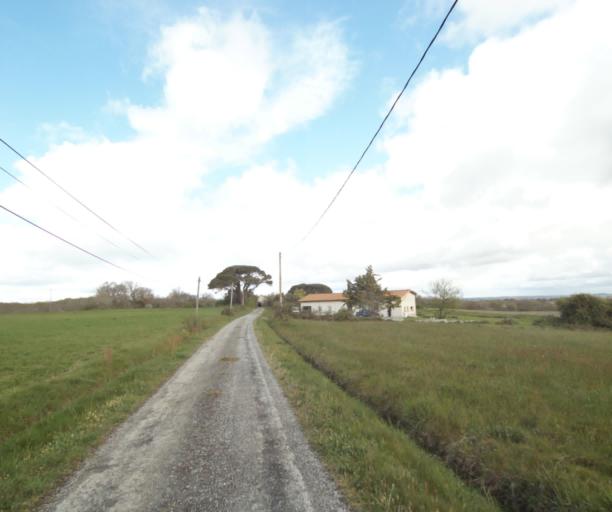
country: FR
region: Midi-Pyrenees
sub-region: Departement de l'Ariege
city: Saverdun
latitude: 43.2317
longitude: 1.5335
